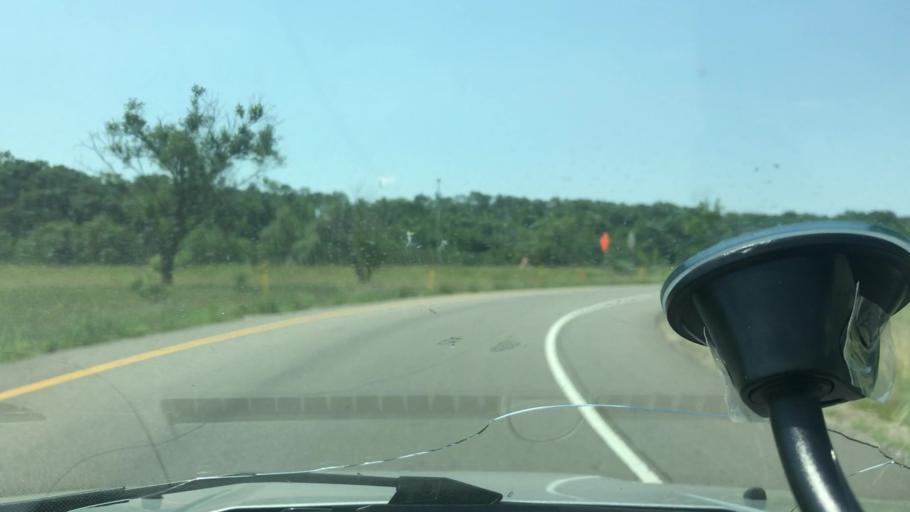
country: US
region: Illinois
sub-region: Tazewell County
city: Marquette Heights
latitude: 40.6306
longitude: -89.6103
